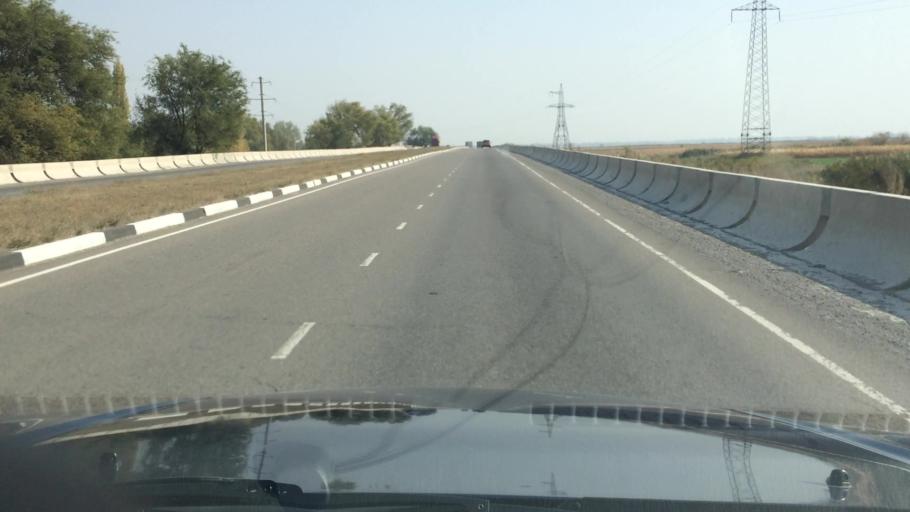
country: KG
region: Chuy
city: Kant
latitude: 42.9672
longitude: 74.8341
